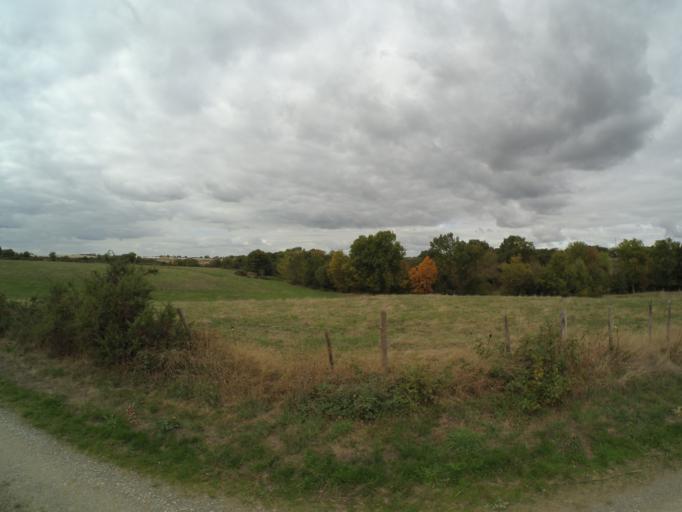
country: FR
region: Pays de la Loire
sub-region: Departement de la Loire-Atlantique
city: Remouille
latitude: 47.0512
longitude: -1.3534
